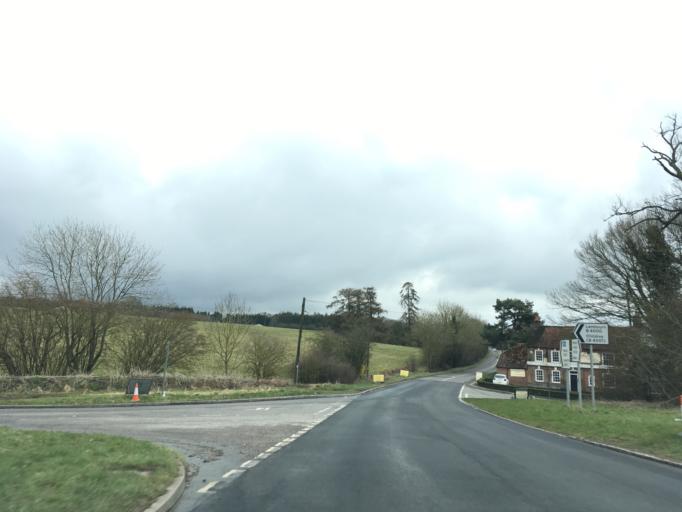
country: GB
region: England
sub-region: West Berkshire
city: Lambourn
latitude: 51.4816
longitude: -1.5436
